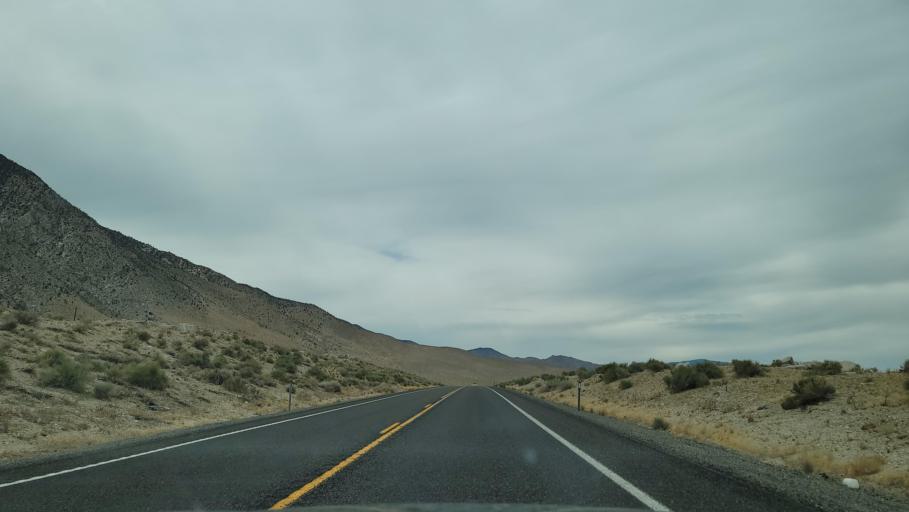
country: US
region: Nevada
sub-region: Mineral County
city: Hawthorne
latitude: 38.5773
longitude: -118.6997
